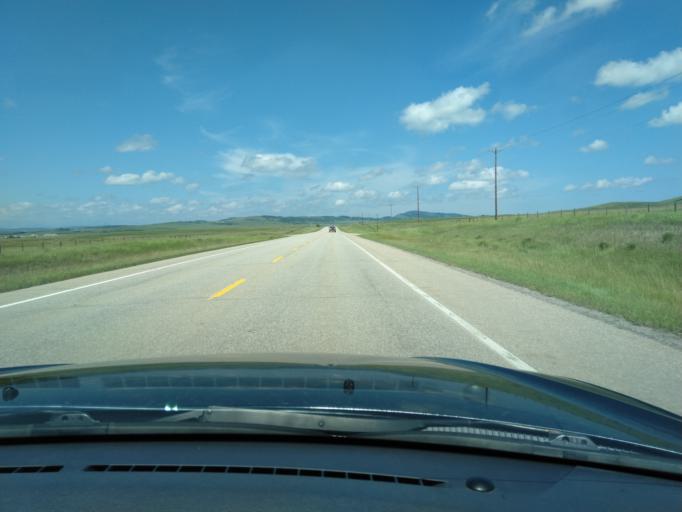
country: CA
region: Alberta
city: Cochrane
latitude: 51.2249
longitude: -114.5523
